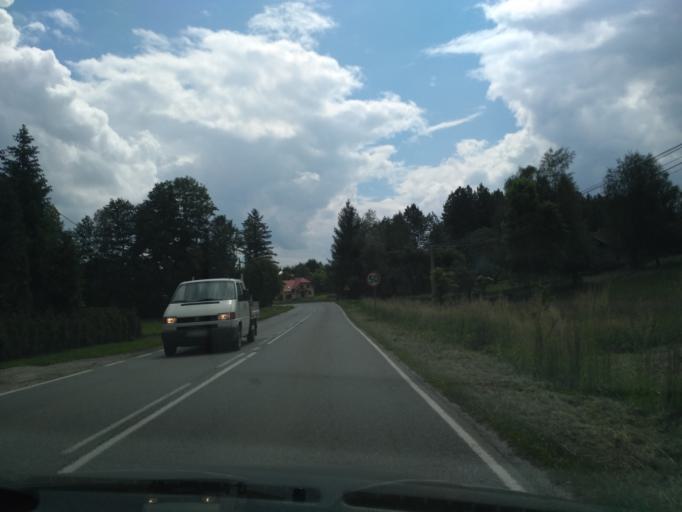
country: PL
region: Subcarpathian Voivodeship
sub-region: Powiat rzeszowski
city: Blazowa
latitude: 49.9272
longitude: 22.1245
